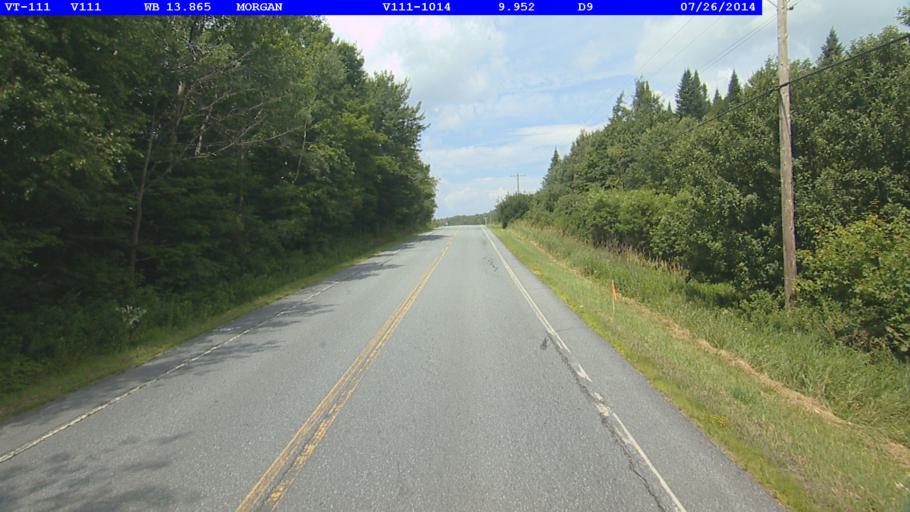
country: US
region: Vermont
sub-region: Orleans County
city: Newport
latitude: 44.8586
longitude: -71.9249
